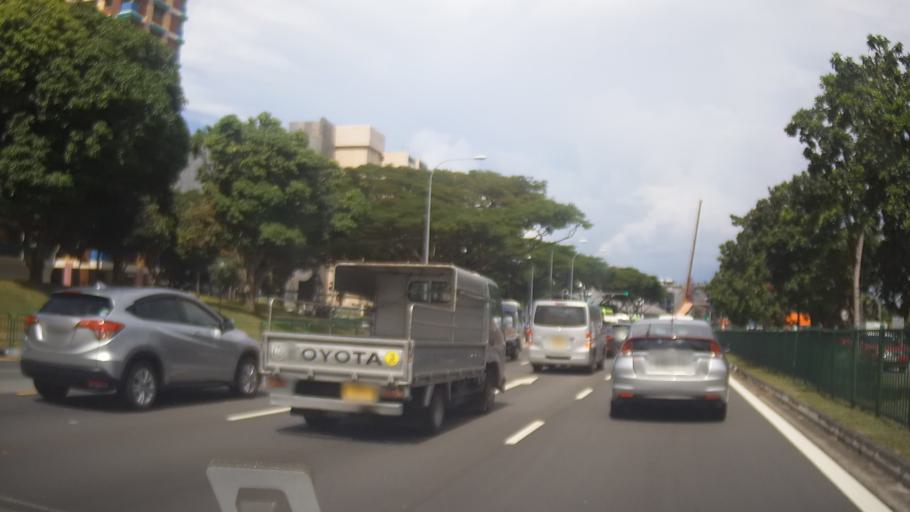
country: SG
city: Singapore
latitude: 1.3302
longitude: 103.9040
